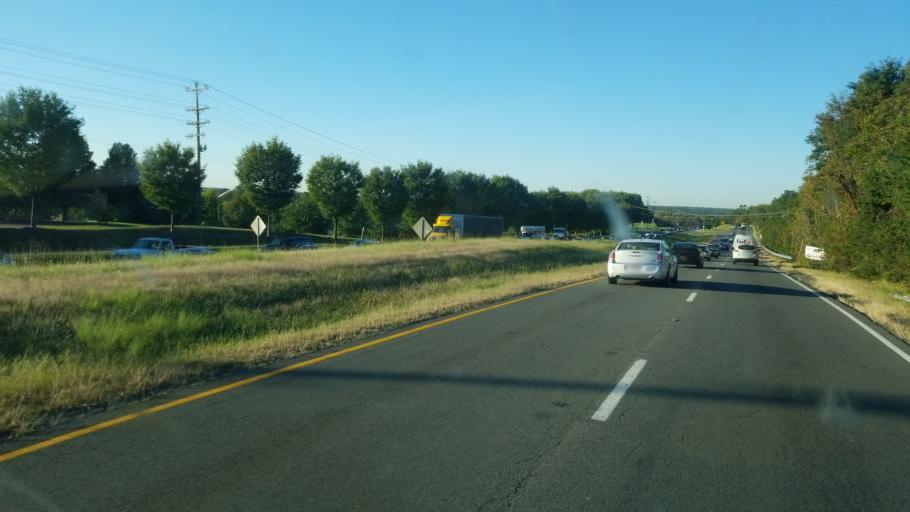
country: US
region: Virginia
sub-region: Prince William County
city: Yorkshire
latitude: 38.8161
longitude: -77.4453
